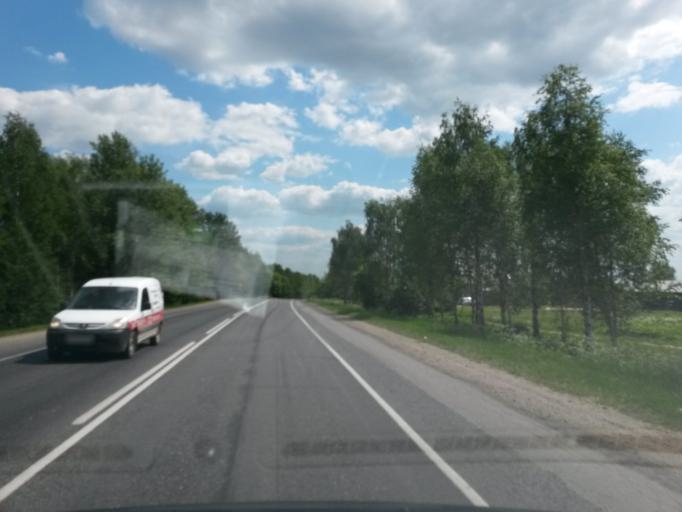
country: RU
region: Jaroslavl
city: Yaroslavl
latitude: 57.5553
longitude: 39.8734
